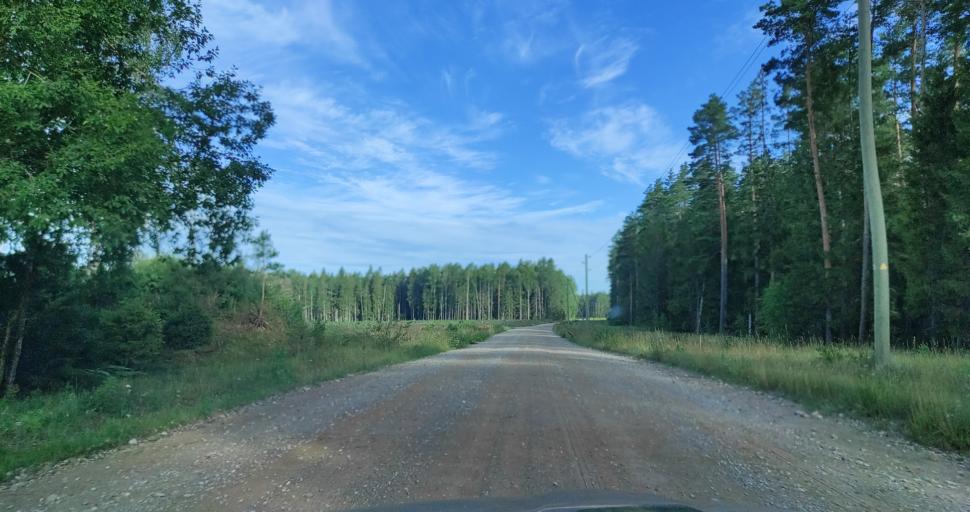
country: LV
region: Durbe
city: Liegi
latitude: 56.7594
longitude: 21.3257
